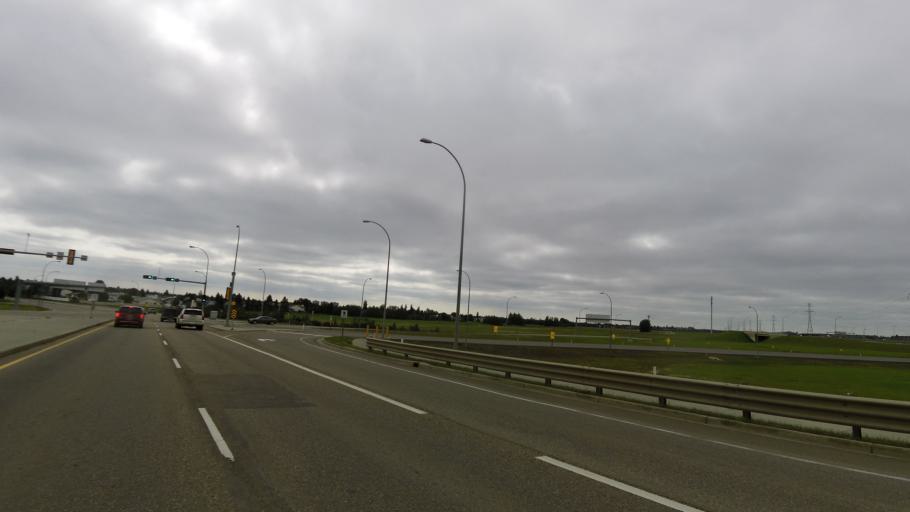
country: CA
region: Alberta
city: St. Albert
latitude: 53.5223
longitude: -113.6565
